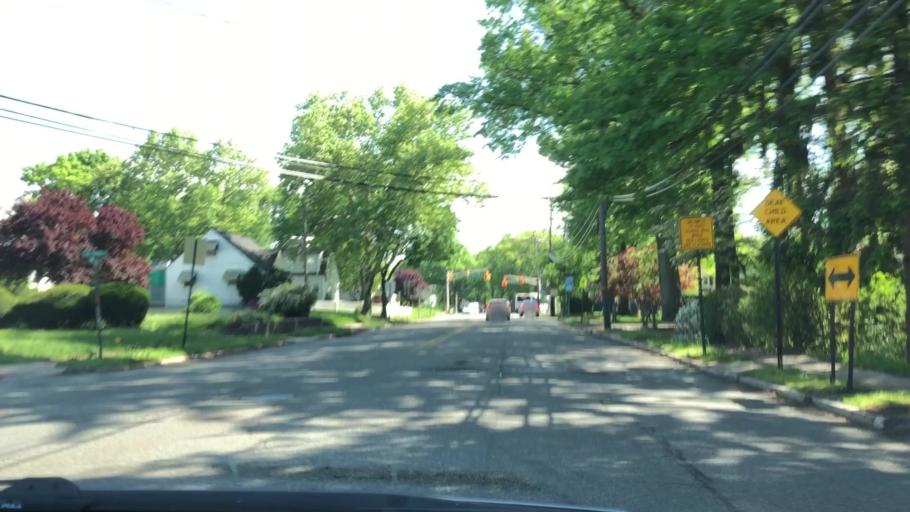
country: US
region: New Jersey
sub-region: Essex County
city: Brookdale
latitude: 40.8298
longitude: -74.1738
